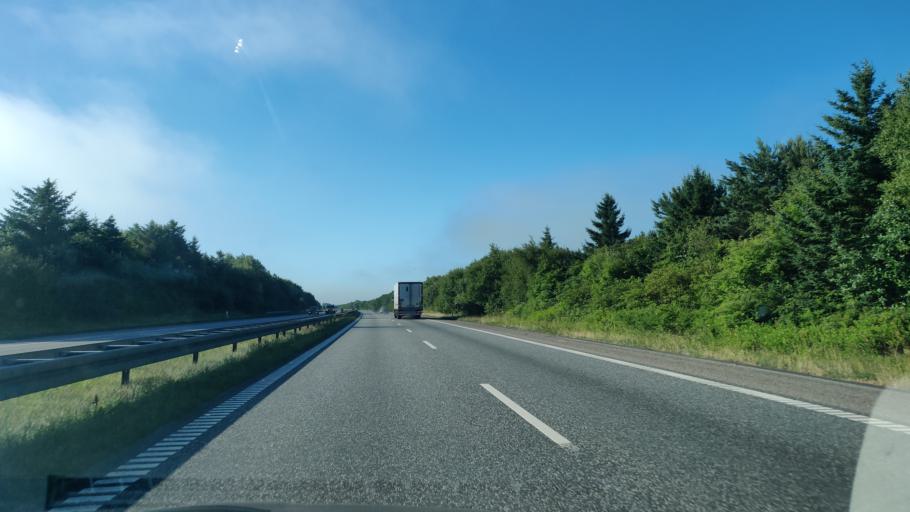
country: DK
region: North Denmark
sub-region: Mariagerfjord Kommune
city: Hobro
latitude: 56.7350
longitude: 9.7037
